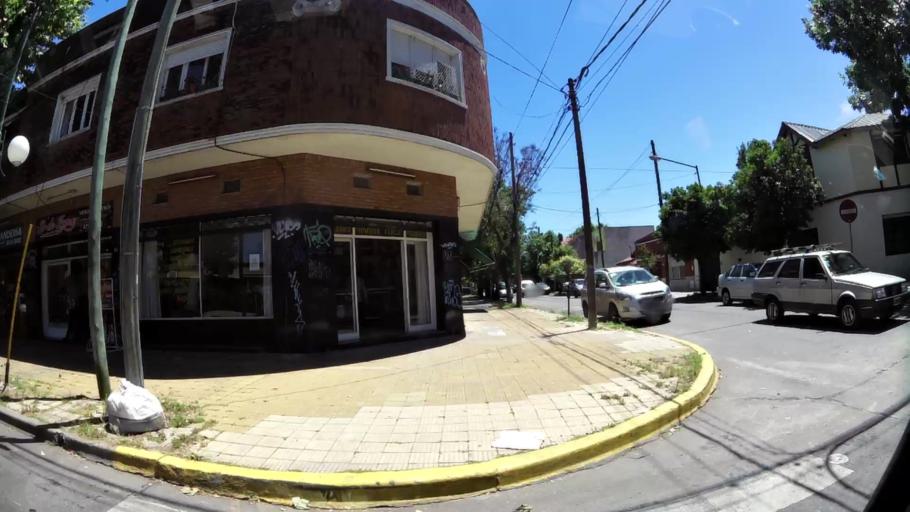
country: AR
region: Buenos Aires
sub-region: Partido de Vicente Lopez
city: Olivos
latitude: -34.4970
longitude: -58.5078
